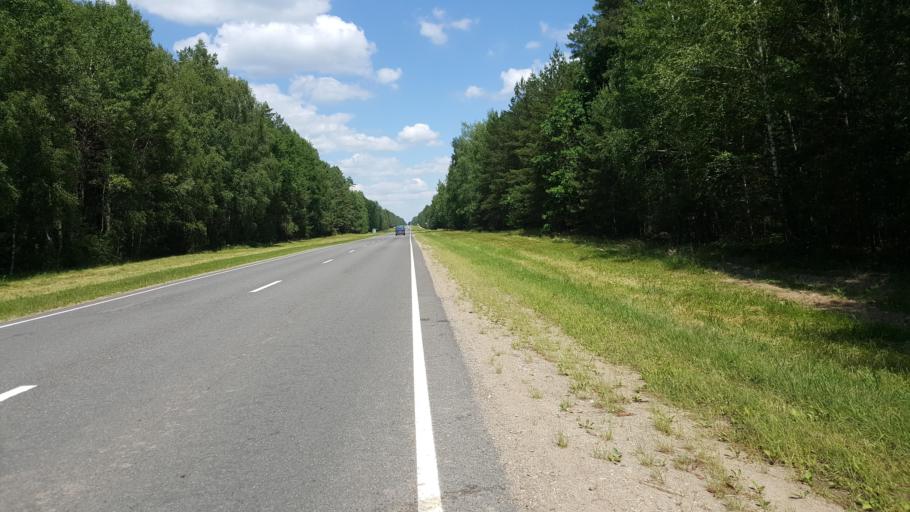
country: BY
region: Brest
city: Kamyanyuki
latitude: 52.5133
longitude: 23.7890
